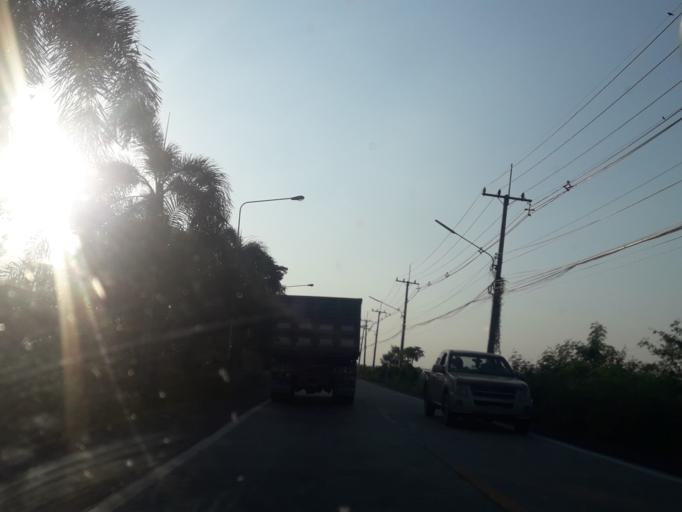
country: TH
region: Pathum Thani
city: Nong Suea
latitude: 14.1361
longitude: 100.8659
